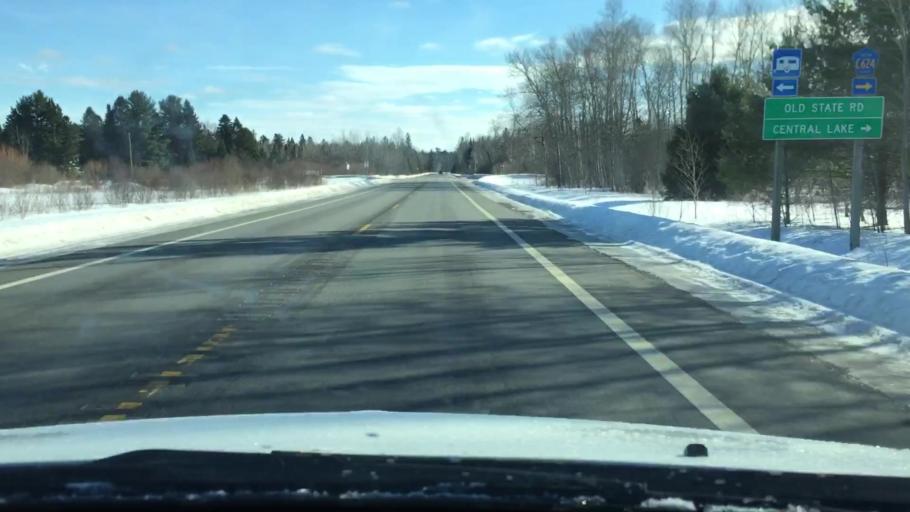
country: US
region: Michigan
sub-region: Charlevoix County
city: East Jordan
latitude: 45.0616
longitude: -85.0789
